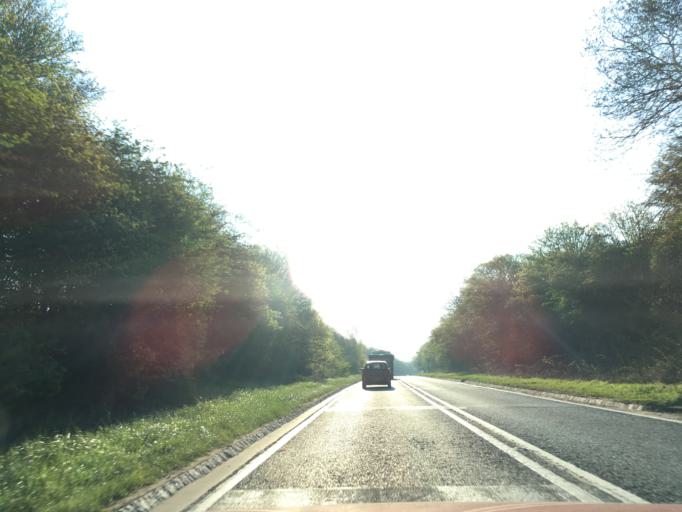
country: GB
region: England
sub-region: Oxfordshire
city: North Leigh
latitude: 51.7910
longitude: -1.4125
